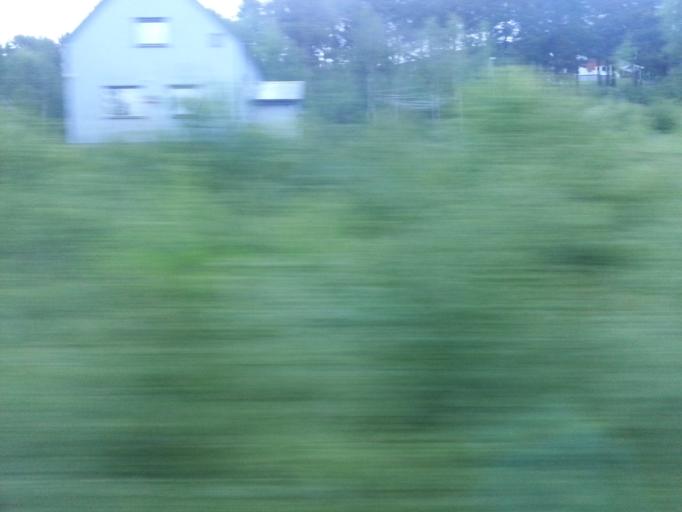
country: NO
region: Oppland
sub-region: Dovre
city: Dombas
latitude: 62.0733
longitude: 9.1289
